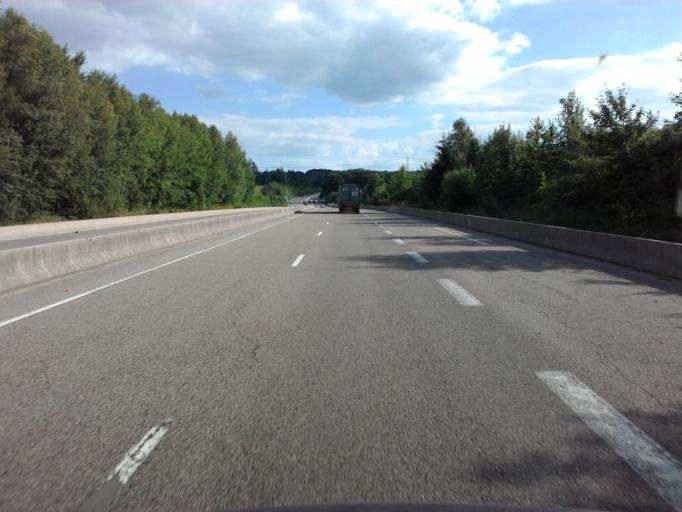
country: FR
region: Lorraine
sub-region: Departement des Vosges
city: Plombieres-les-Bains
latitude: 47.9739
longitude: 6.4940
